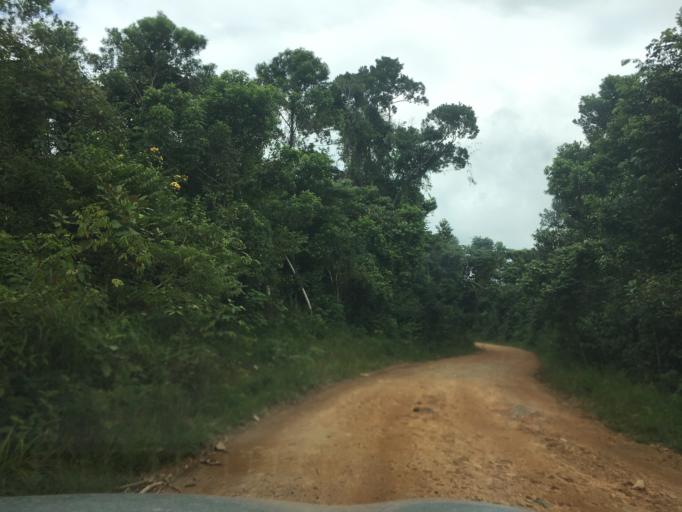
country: BZ
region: Stann Creek
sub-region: Dangriga
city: Dangriga
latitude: 16.9324
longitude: -88.3532
